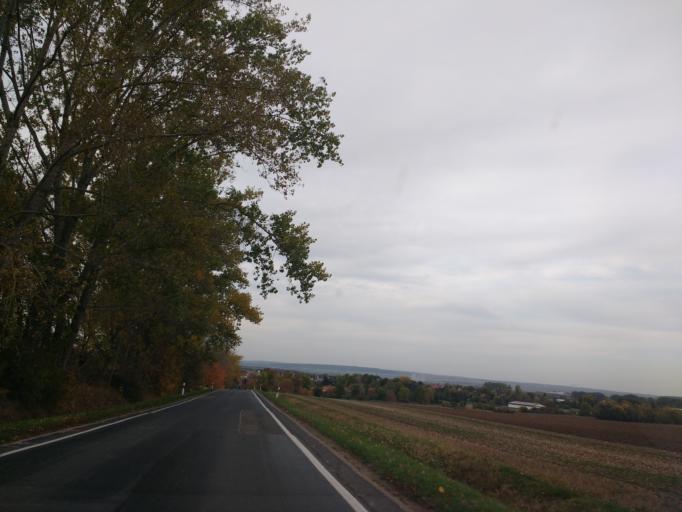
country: DE
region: Thuringia
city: Seebach
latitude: 51.1581
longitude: 10.5176
